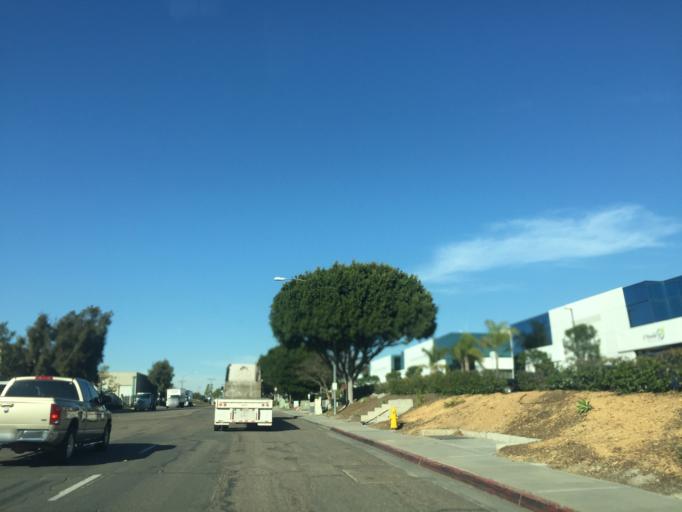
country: MX
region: Baja California
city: Tijuana
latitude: 32.5582
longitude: -116.9358
